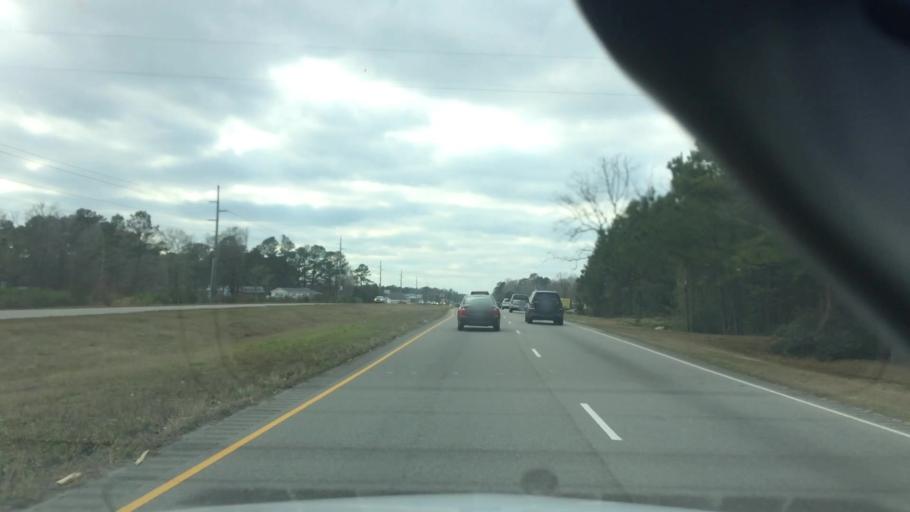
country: US
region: North Carolina
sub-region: Brunswick County
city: Shallotte
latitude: 34.0153
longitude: -78.2790
